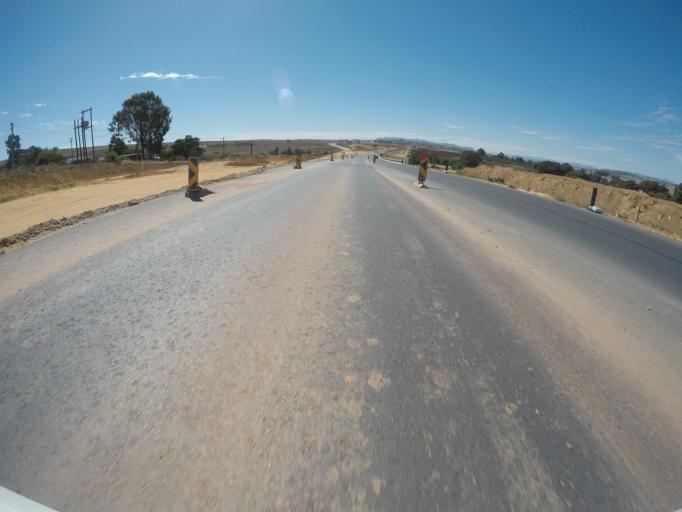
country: ZA
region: Western Cape
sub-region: West Coast District Municipality
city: Malmesbury
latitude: -33.4853
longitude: 18.6741
